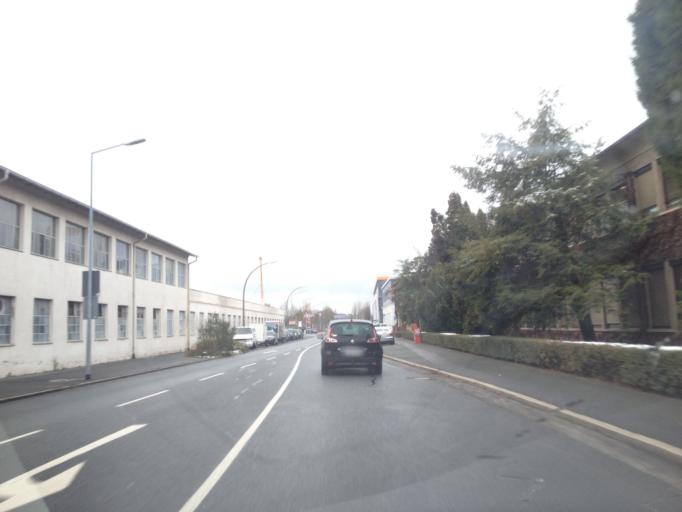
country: DE
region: Bavaria
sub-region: Regierungsbezirk Mittelfranken
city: Lauf an der Pegnitz
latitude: 49.5069
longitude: 11.2705
